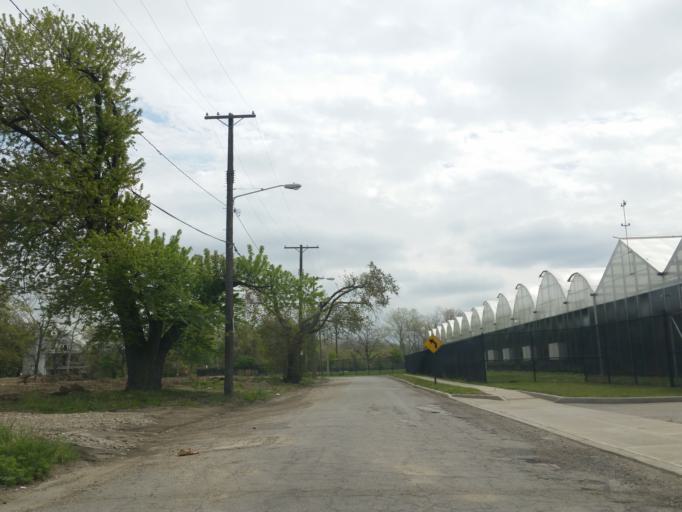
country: US
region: Ohio
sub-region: Cuyahoga County
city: Newburgh Heights
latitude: 41.4847
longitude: -81.6503
